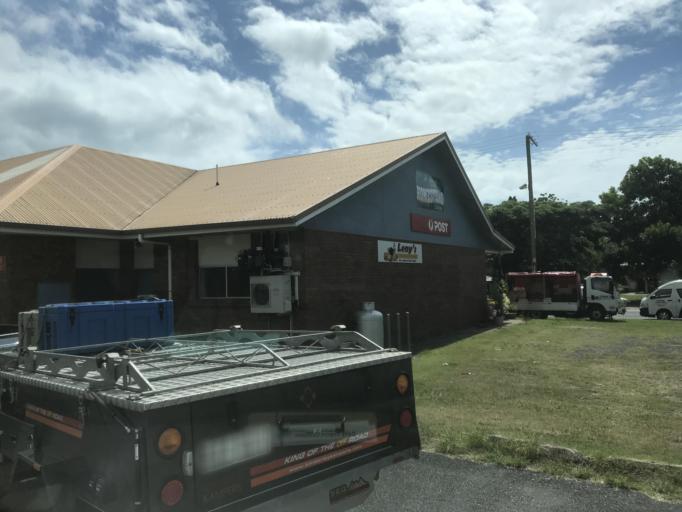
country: AU
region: Queensland
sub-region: Cassowary Coast
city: Innisfail
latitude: -17.8677
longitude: 146.1066
